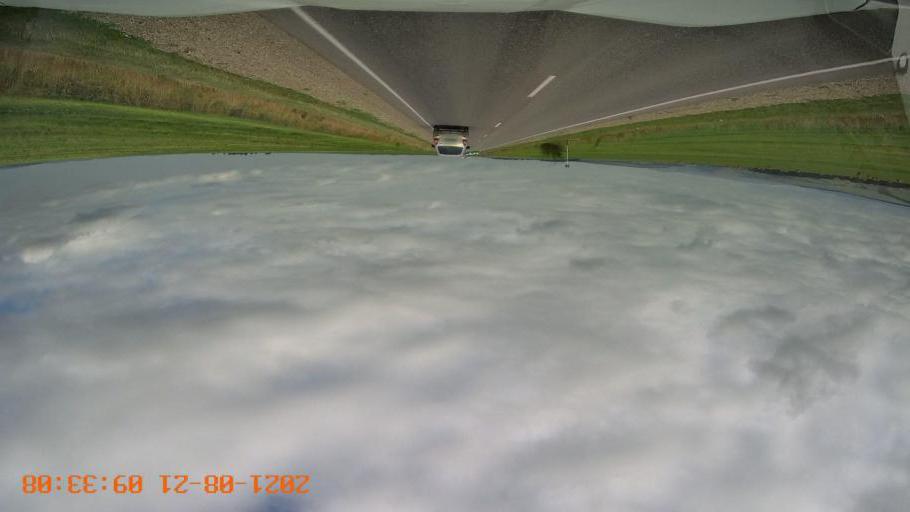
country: RU
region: Stavropol'skiy
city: Yutsa
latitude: 43.9927
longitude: 42.9950
